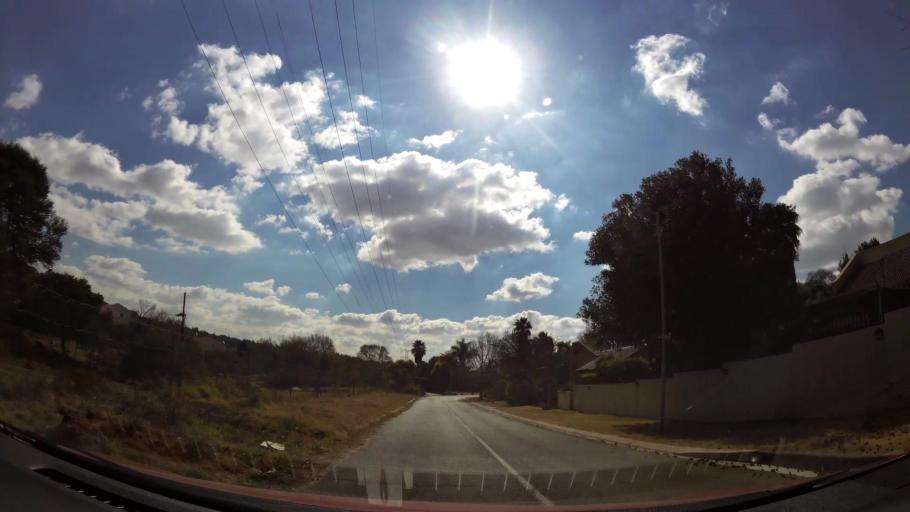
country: ZA
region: Gauteng
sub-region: City of Johannesburg Metropolitan Municipality
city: Roodepoort
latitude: -26.0743
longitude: 27.9654
